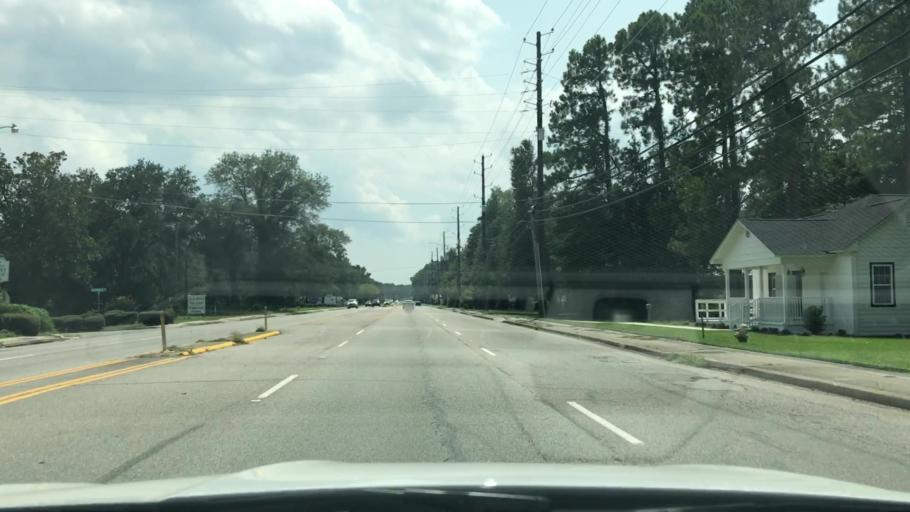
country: US
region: South Carolina
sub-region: Georgetown County
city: Georgetown
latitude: 33.4071
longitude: -79.2873
